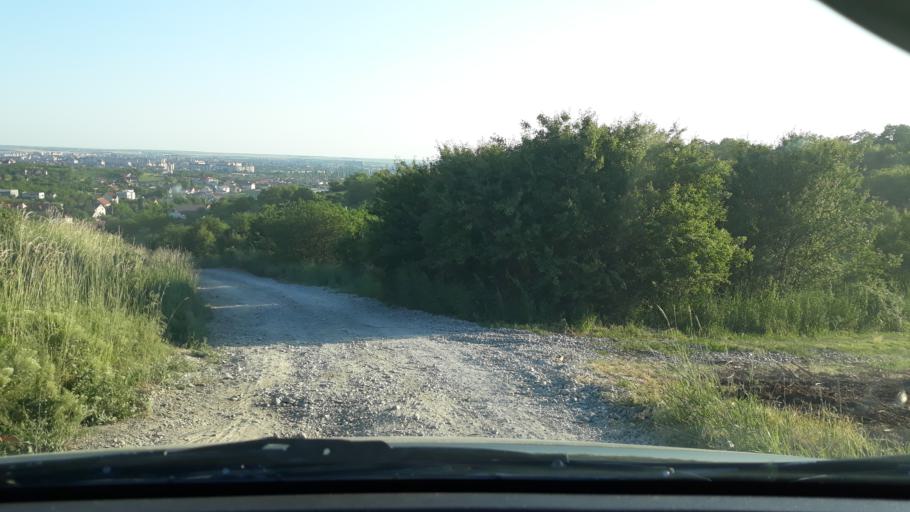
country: RO
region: Bihor
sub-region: Comuna Paleu
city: Paleu
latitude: 47.1019
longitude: 21.9356
